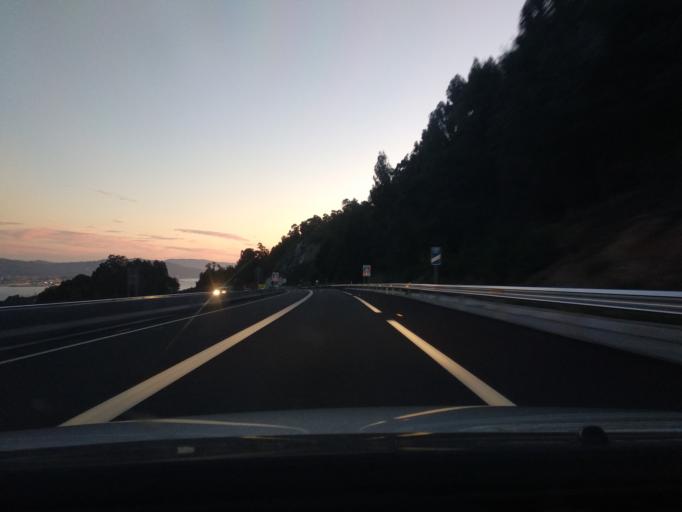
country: ES
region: Galicia
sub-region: Provincia de Pontevedra
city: Moana
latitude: 42.2934
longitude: -8.7525
